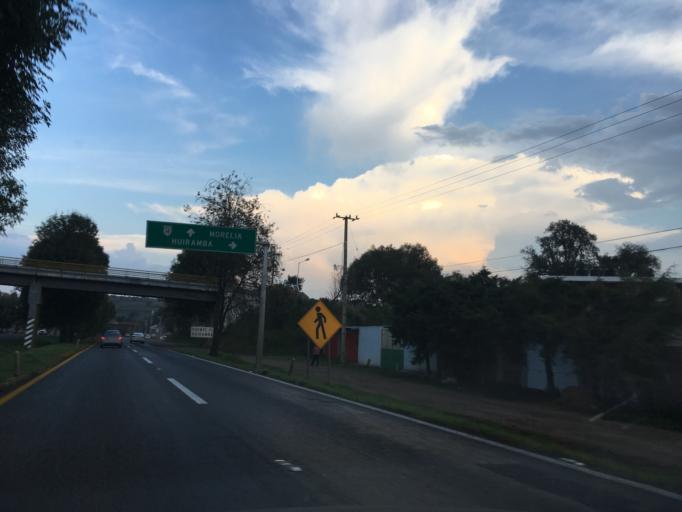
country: MX
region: Michoacan
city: Huiramba
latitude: 19.5471
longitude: -101.4417
